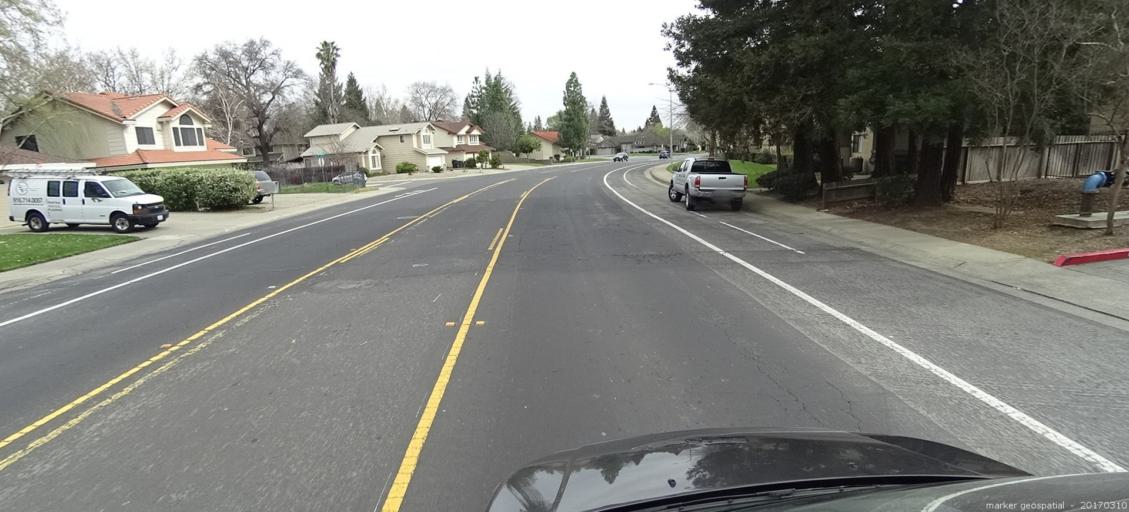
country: US
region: California
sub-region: Sacramento County
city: Parkway
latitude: 38.4833
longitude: -121.5193
